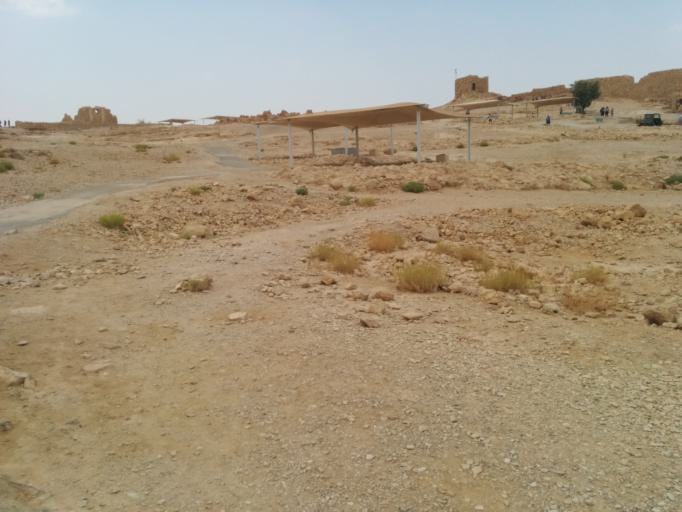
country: IL
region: Southern District
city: `En Boqeq
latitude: 31.3158
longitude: 35.3550
